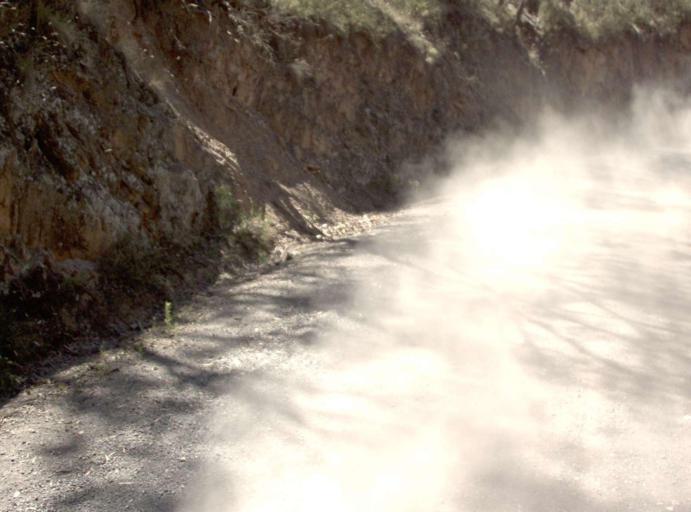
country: AU
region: New South Wales
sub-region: Bombala
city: Bombala
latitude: -37.0997
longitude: 148.6336
